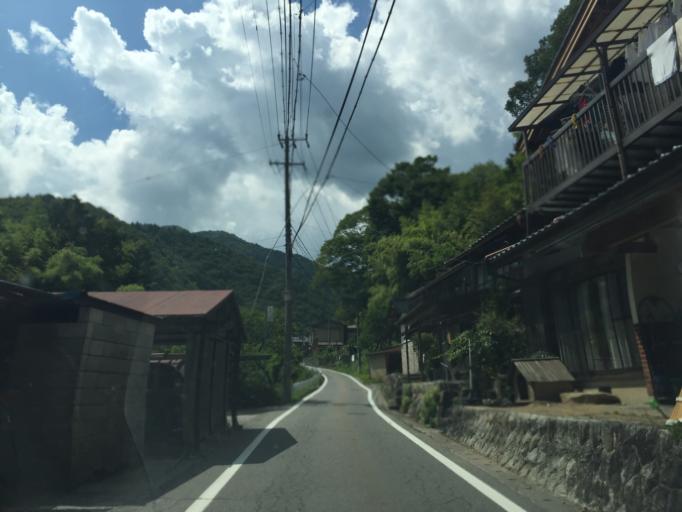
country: JP
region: Nagano
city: Iida
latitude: 35.3759
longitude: 137.6895
